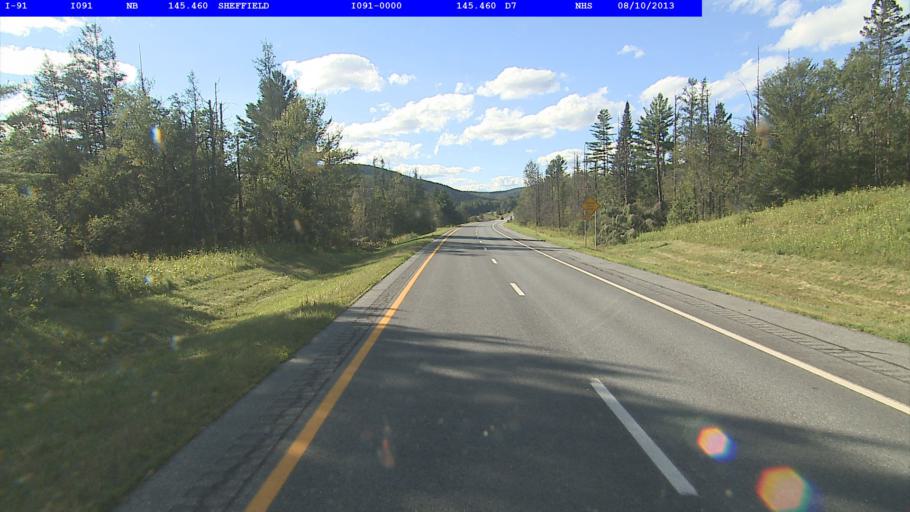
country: US
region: Vermont
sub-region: Caledonia County
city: Lyndonville
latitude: 44.6030
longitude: -72.1088
